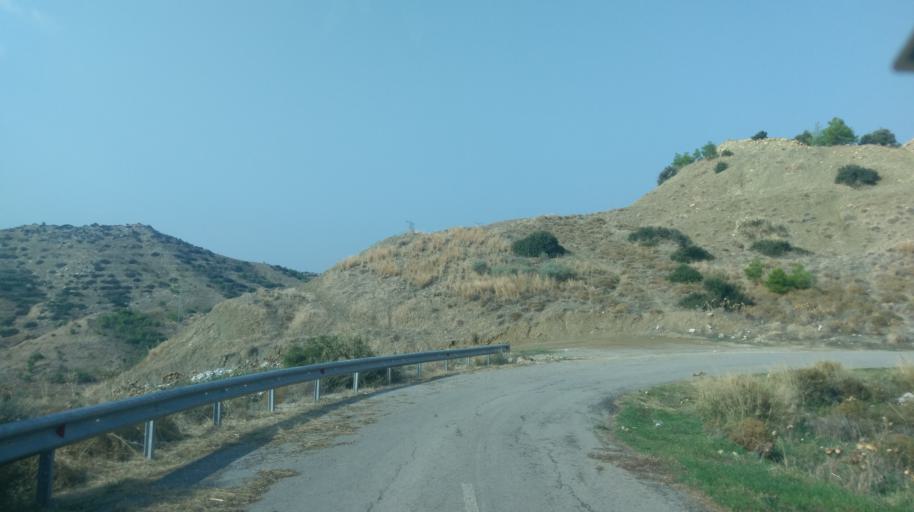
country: CY
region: Keryneia
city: Kyrenia
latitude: 35.3130
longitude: 33.4662
